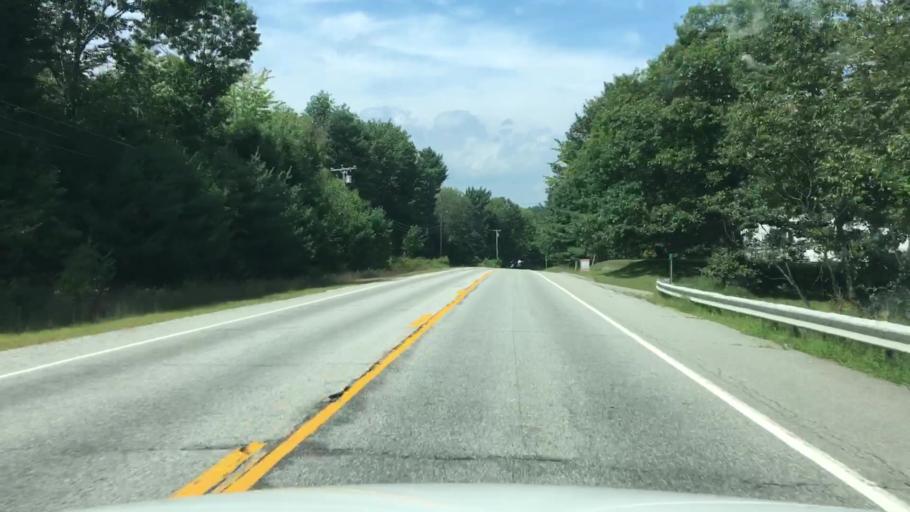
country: US
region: Maine
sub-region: Oxford County
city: Peru
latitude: 44.4996
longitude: -70.3970
